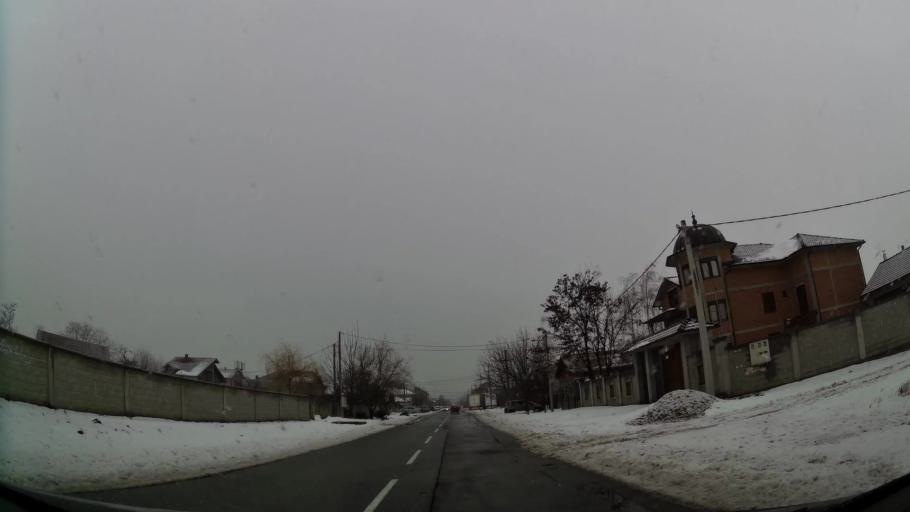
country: RS
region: Central Serbia
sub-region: Belgrade
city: Zemun
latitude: 44.8532
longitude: 20.3343
